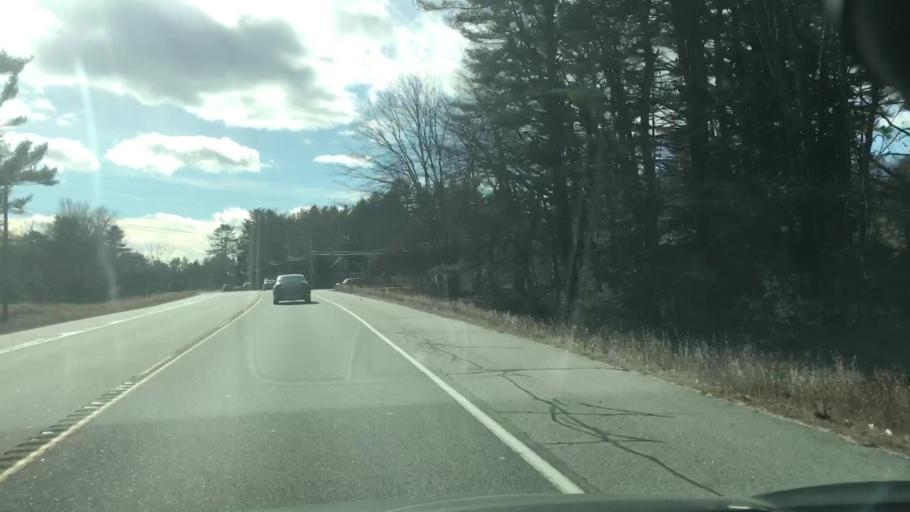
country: US
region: New Hampshire
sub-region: Merrimack County
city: Chichester
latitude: 43.2742
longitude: -71.3677
